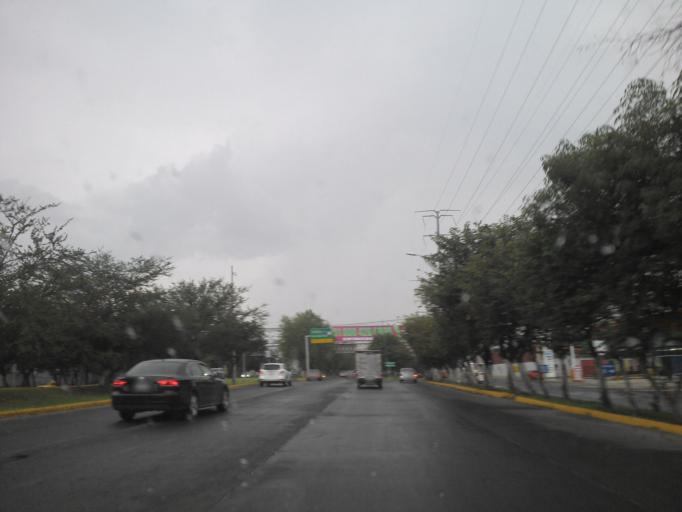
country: MX
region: Jalisco
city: Tlaquepaque
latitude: 20.6249
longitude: -103.3066
